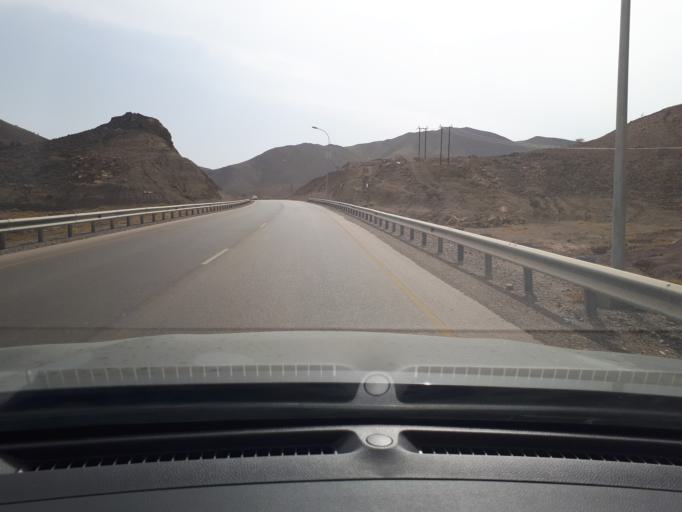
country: OM
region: Ash Sharqiyah
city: Badiyah
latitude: 22.5370
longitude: 58.9774
